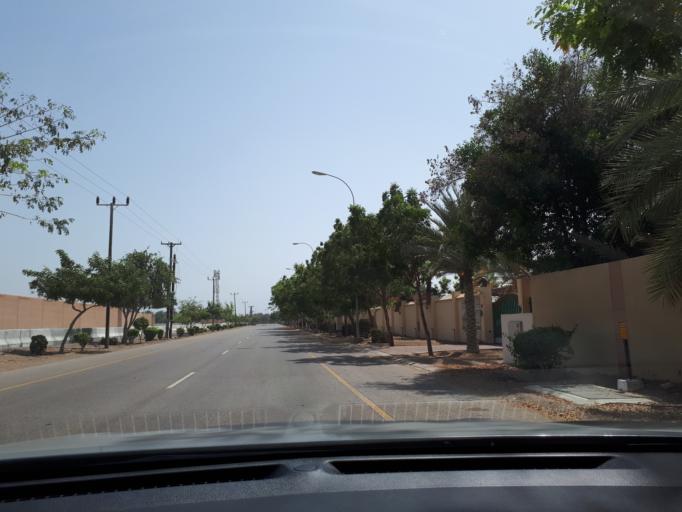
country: OM
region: Muhafazat Masqat
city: As Sib al Jadidah
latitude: 23.6982
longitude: 58.0740
